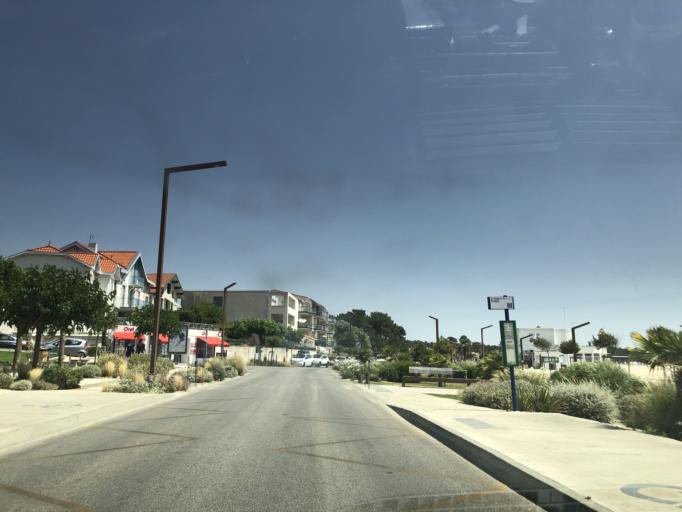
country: FR
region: Poitou-Charentes
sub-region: Departement de la Charente-Maritime
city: Saint-Georges-de-Didonne
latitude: 45.6012
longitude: -0.9986
